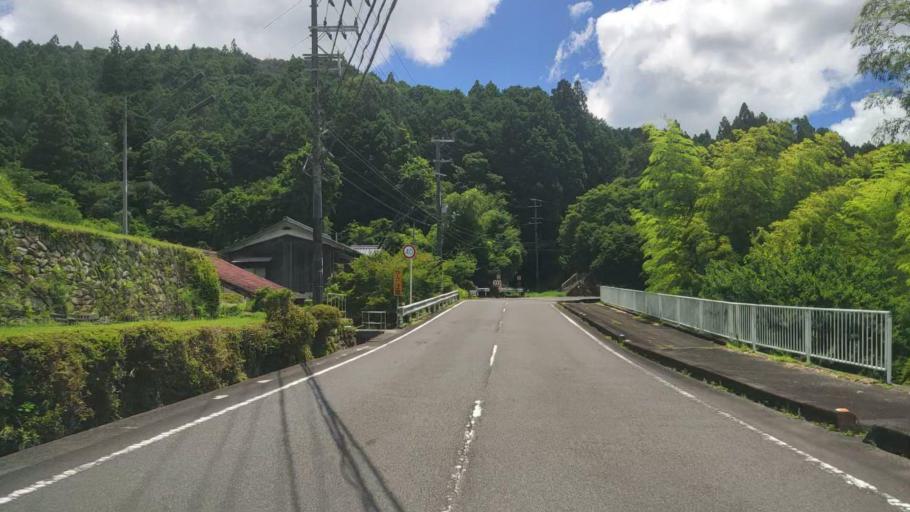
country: JP
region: Mie
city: Owase
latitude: 33.9573
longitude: 136.0699
